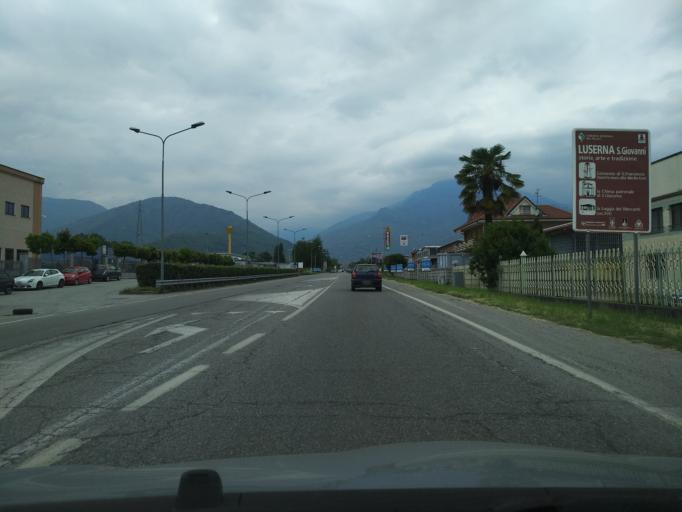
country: IT
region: Piedmont
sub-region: Provincia di Torino
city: Bibiana
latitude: 44.8110
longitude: 7.2736
